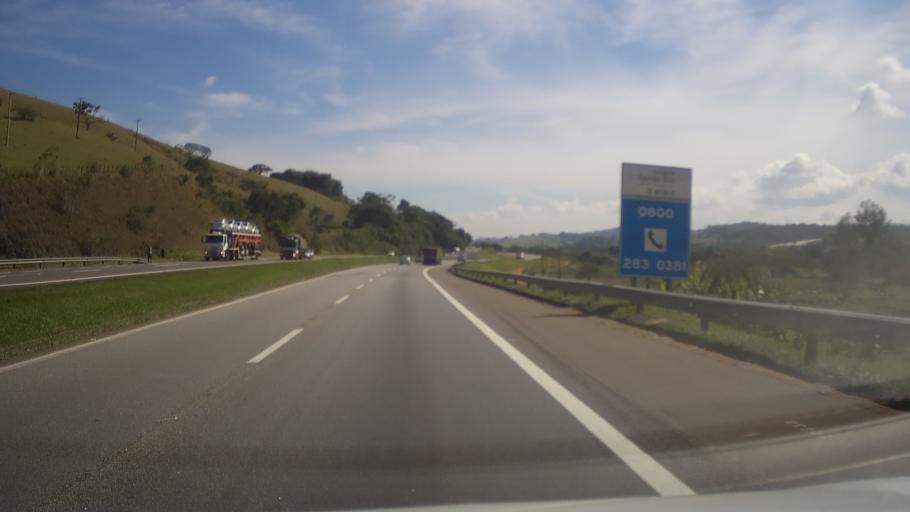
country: BR
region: Minas Gerais
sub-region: Cambui
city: Cambui
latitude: -22.5817
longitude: -46.0456
